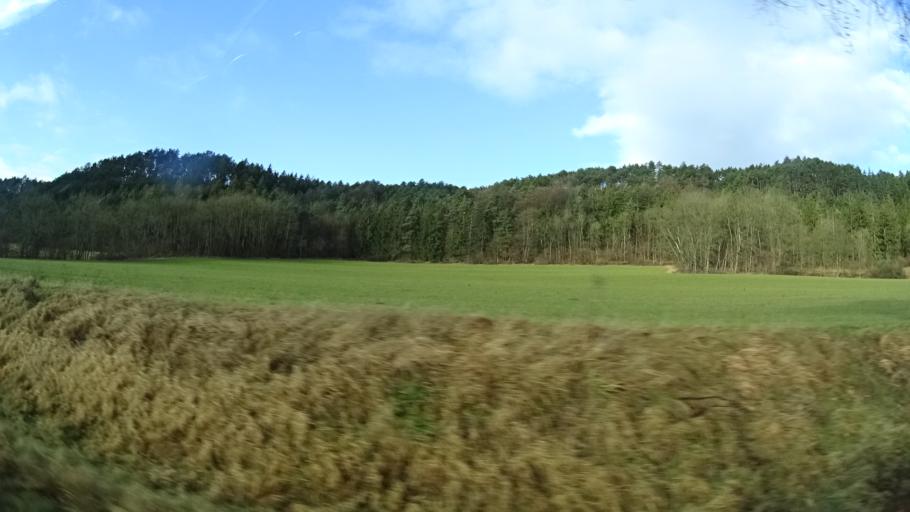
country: DE
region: Thuringia
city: Arnstadt
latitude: 50.8112
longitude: 10.9338
